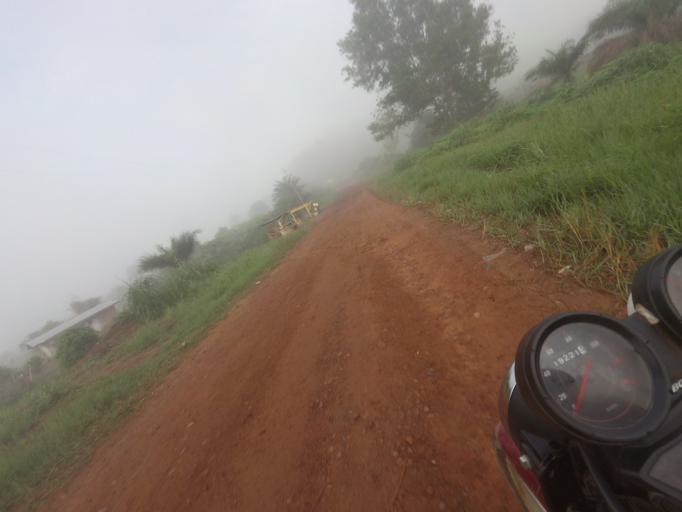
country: LR
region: Nimba
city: New Yekepa
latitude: 7.5663
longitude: -8.5523
